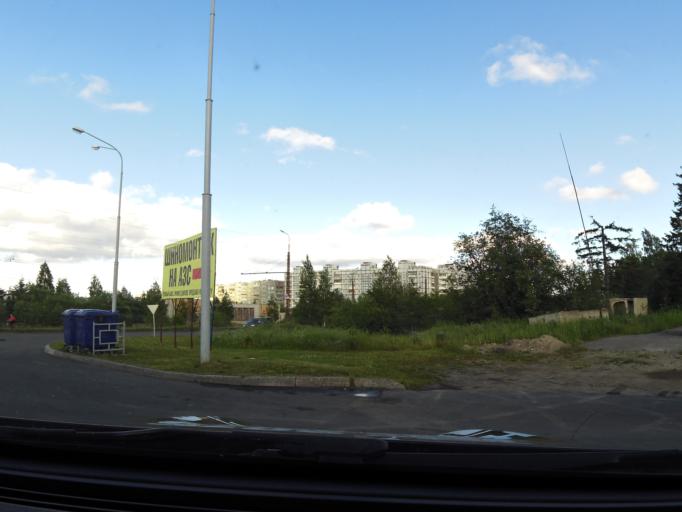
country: RU
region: Republic of Karelia
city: Petrozavodsk
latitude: 61.7641
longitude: 34.4144
